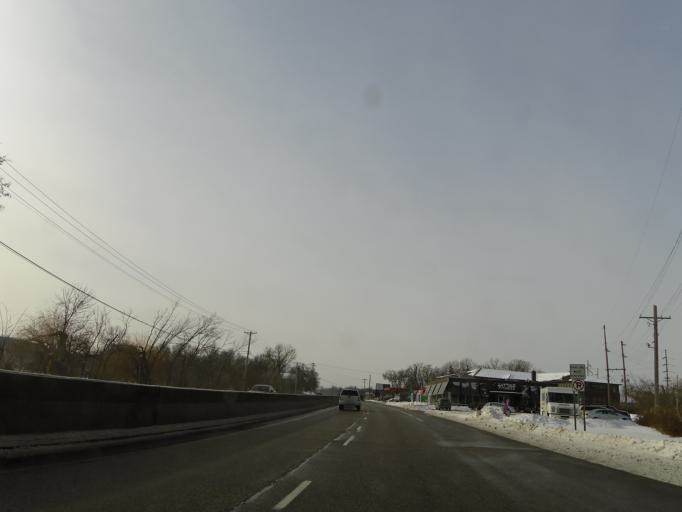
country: US
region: Minnesota
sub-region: Hennepin County
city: Excelsior
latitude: 44.9005
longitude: -93.5623
